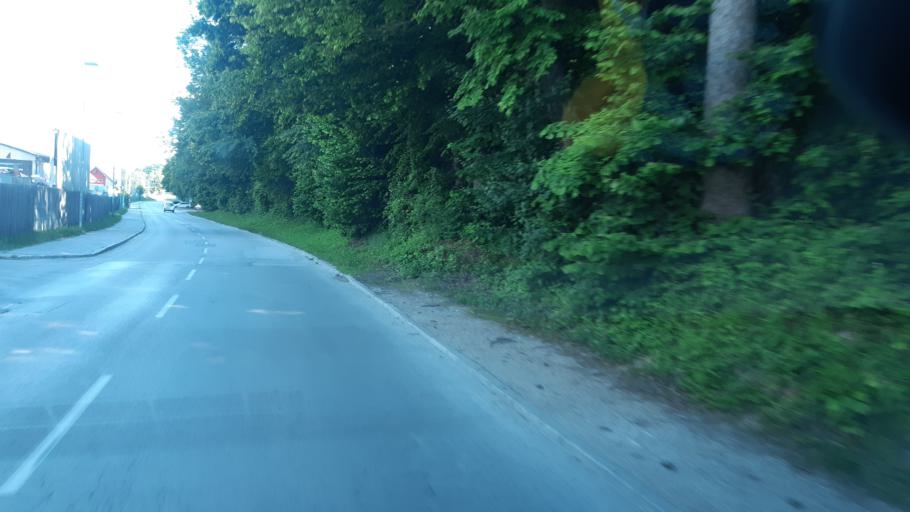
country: SI
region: Kranj
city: Kranj
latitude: 46.2245
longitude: 14.3630
